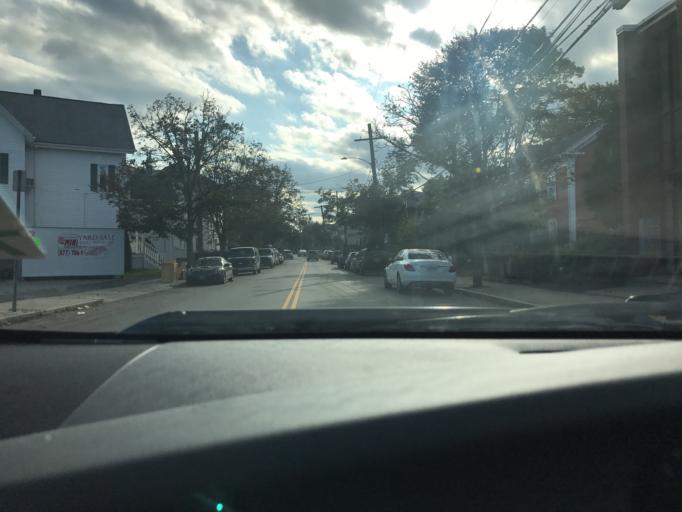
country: US
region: Massachusetts
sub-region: Middlesex County
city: Waltham
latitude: 42.3709
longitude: -71.2399
